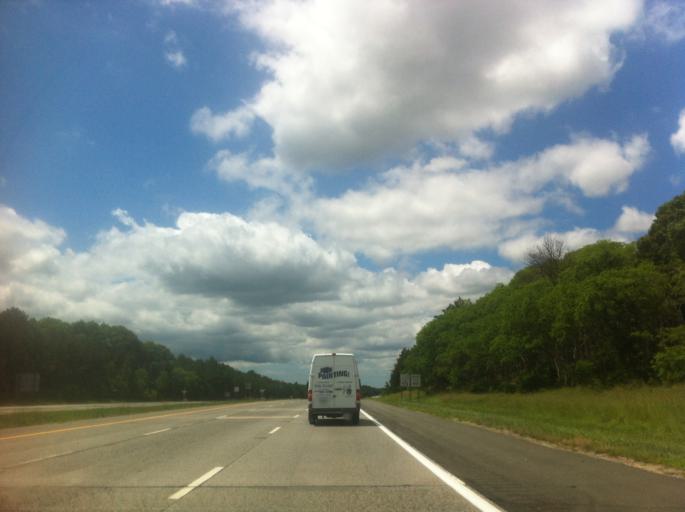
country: US
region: New York
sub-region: Suffolk County
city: Calverton
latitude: 40.8959
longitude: -72.7474
